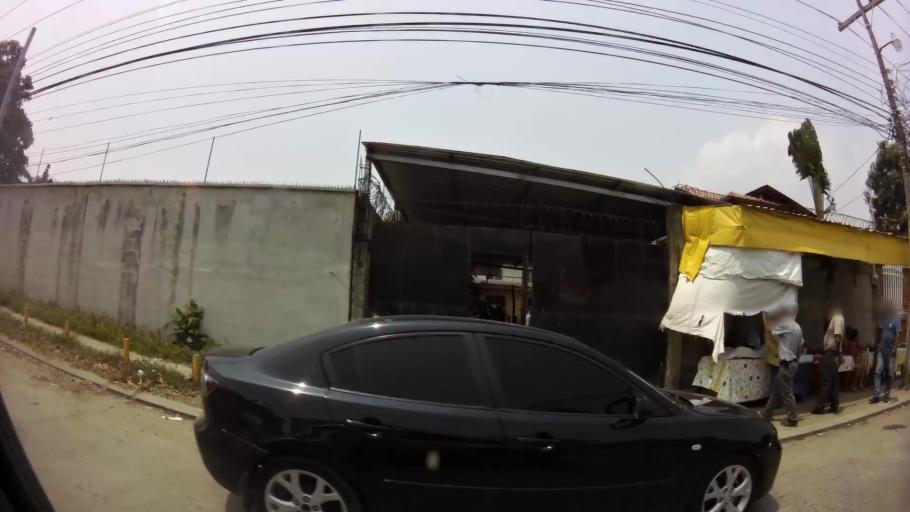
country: HN
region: Cortes
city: San Pedro Sula
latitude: 15.4882
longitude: -88.0011
